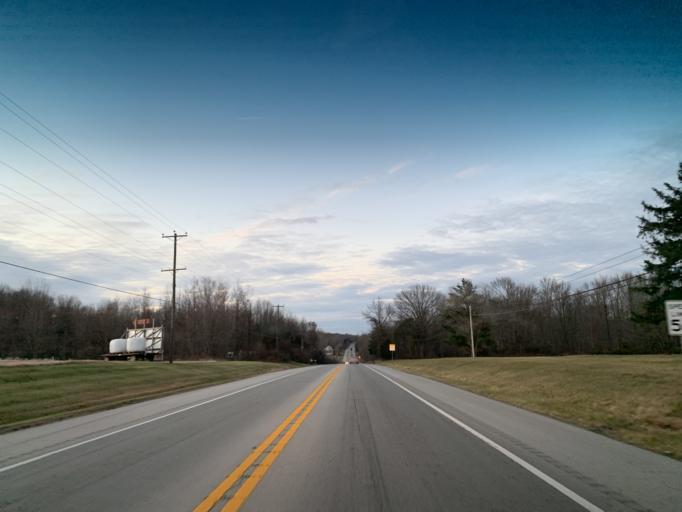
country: US
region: Maryland
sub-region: Cecil County
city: Elkton
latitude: 39.5676
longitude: -75.8119
